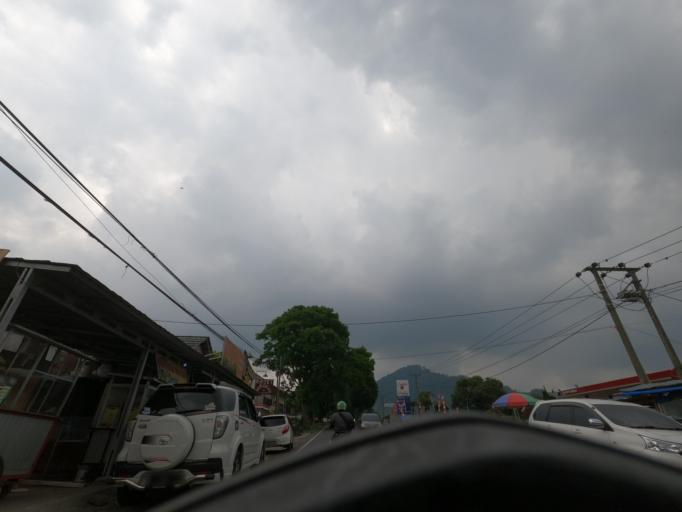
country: ID
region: West Java
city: Sukabumi
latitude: -6.7749
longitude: 107.0636
